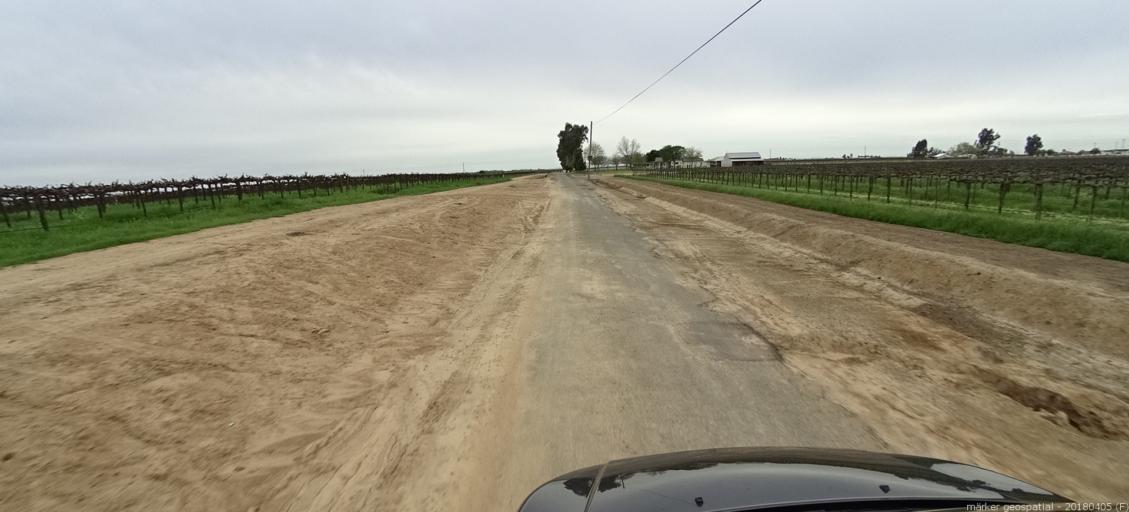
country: US
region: California
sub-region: Sacramento County
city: Herald
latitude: 38.3175
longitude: -121.2386
